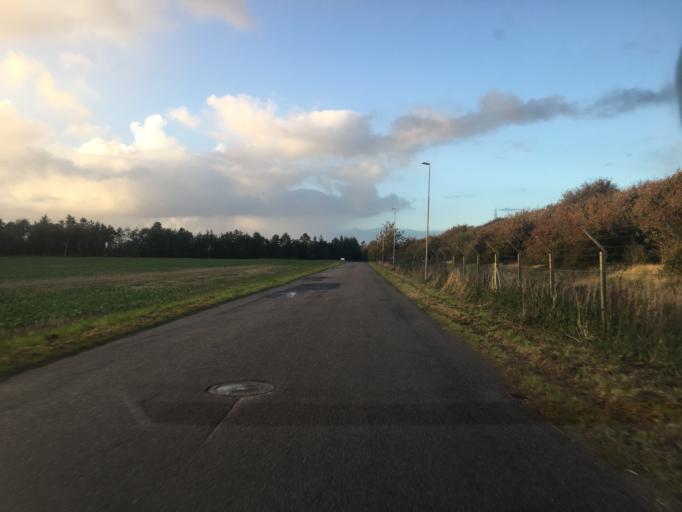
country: DK
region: South Denmark
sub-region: Tonder Kommune
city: Tonder
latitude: 54.9241
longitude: 8.8510
